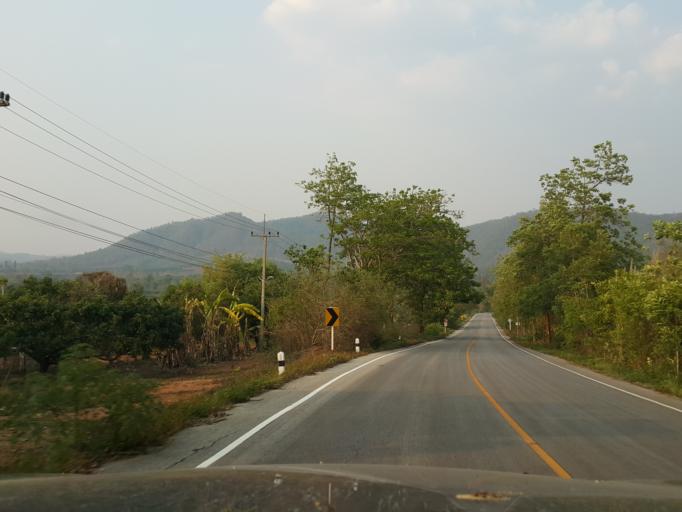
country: TH
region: Lamphun
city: Li
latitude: 17.8431
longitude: 98.9935
